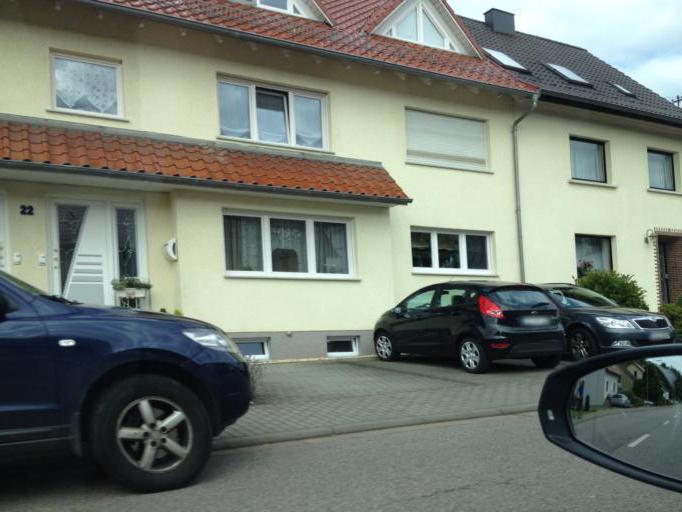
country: DE
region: Saarland
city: Lebach
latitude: 49.4497
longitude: 6.8983
